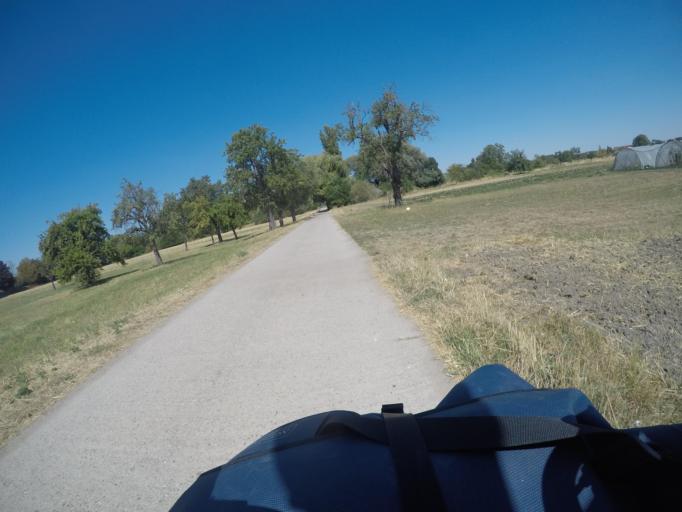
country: DE
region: Baden-Wuerttemberg
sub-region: Karlsruhe Region
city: Altlussheim
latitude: 49.3011
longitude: 8.4915
